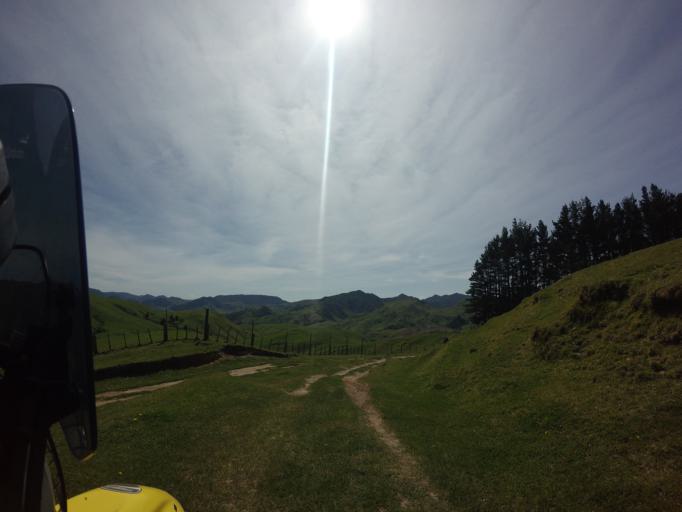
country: NZ
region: Bay of Plenty
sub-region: Opotiki District
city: Opotiki
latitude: -38.4713
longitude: 177.3788
